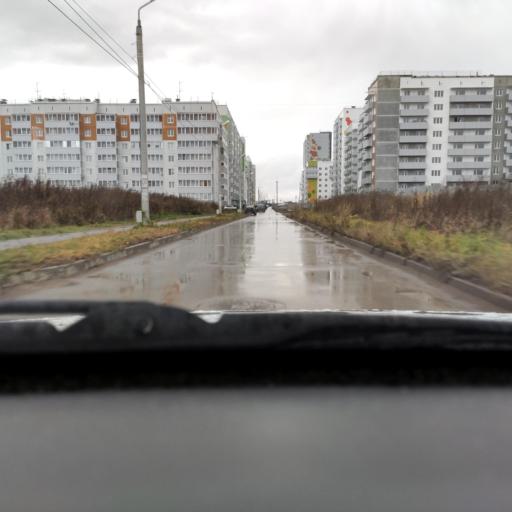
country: RU
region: Perm
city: Kondratovo
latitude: 57.9869
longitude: 56.1221
